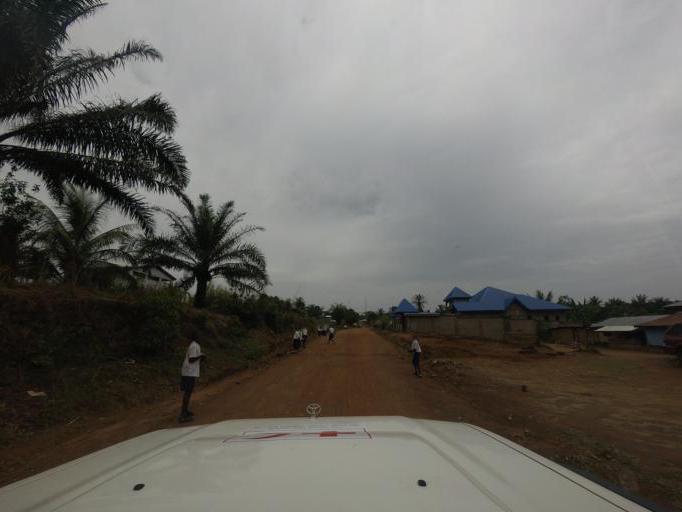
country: SL
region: Eastern Province
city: Buedu
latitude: 8.3517
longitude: -10.2088
